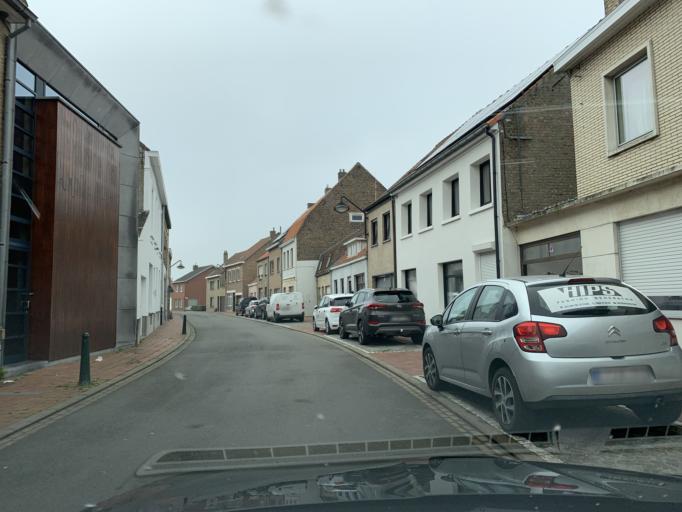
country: BE
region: Flanders
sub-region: Provincie West-Vlaanderen
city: De Panne
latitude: 51.0748
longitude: 2.6007
